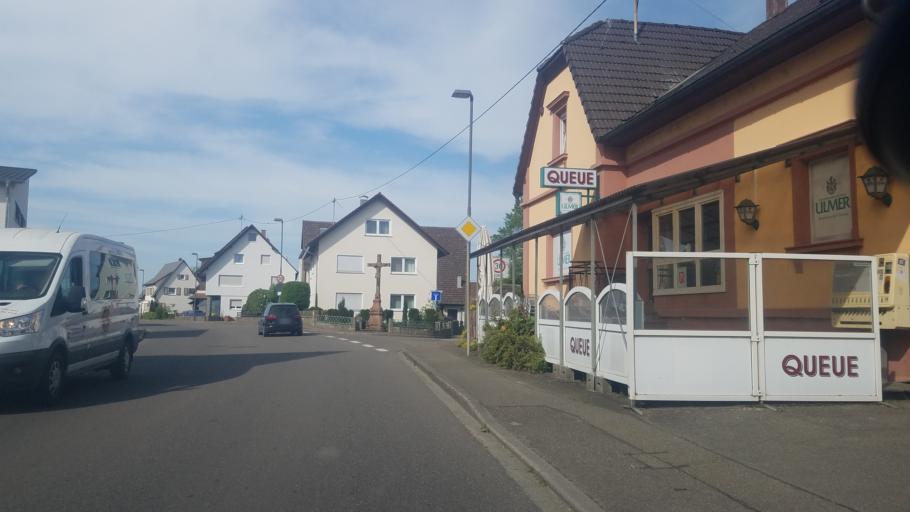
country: DE
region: Baden-Wuerttemberg
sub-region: Freiburg Region
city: Meissenheim
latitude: 48.4354
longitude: 7.8131
